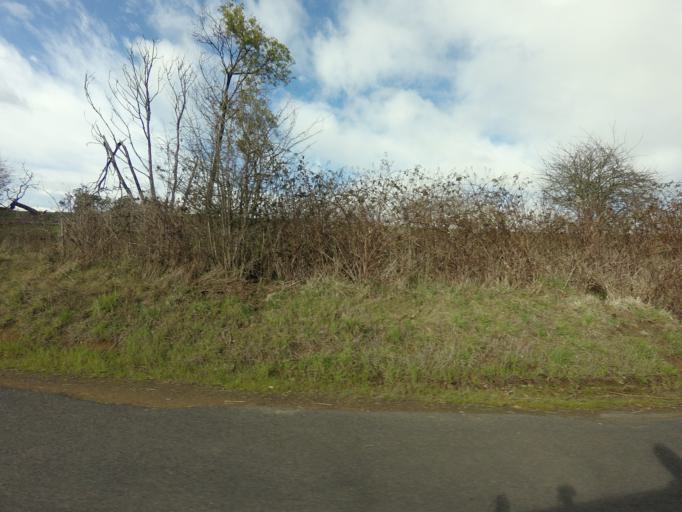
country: AU
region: Tasmania
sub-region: Derwent Valley
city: New Norfolk
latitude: -42.7112
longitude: 146.8945
